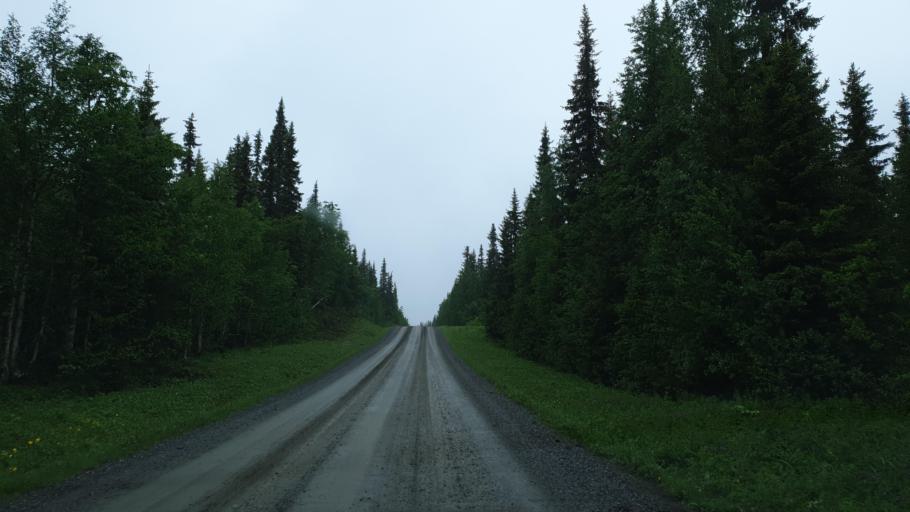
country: SE
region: Vaesterbotten
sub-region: Vilhelmina Kommun
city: Sjoberg
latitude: 65.2639
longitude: 15.9412
